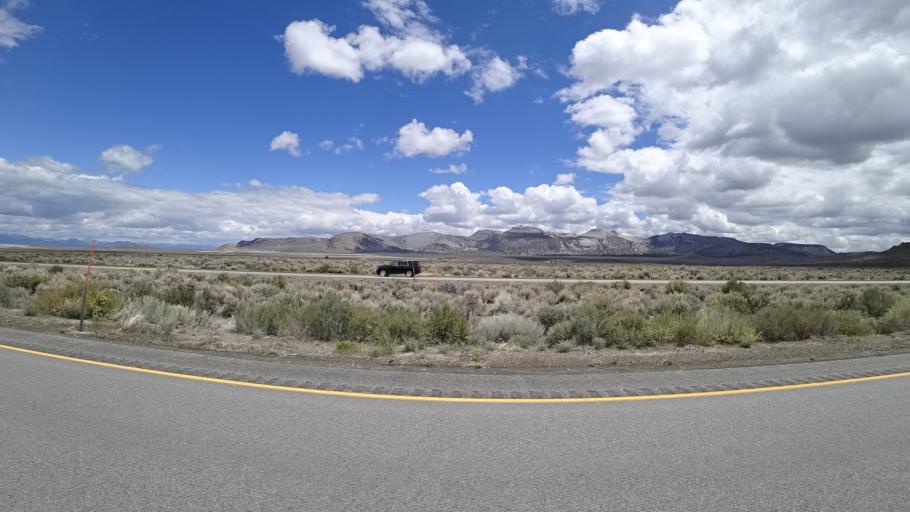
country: US
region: California
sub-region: Mono County
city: Mammoth Lakes
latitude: 37.8775
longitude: -119.0895
